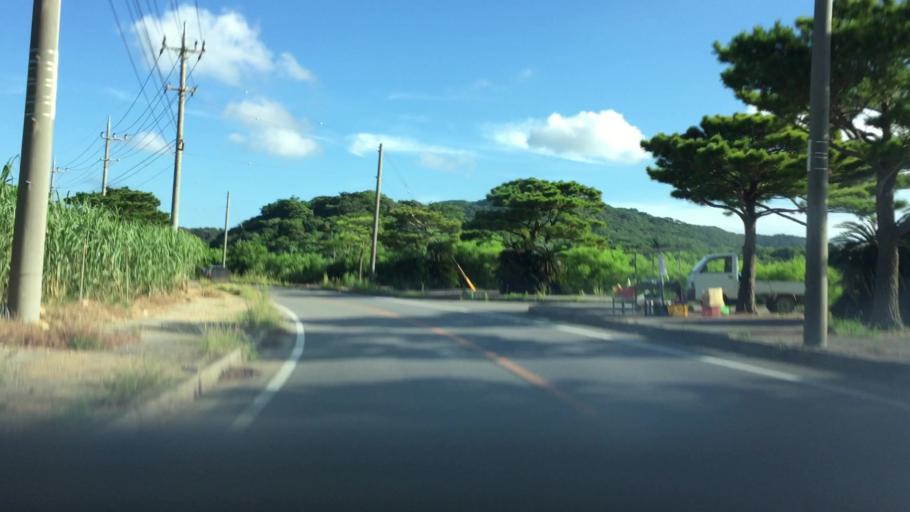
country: JP
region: Okinawa
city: Ishigaki
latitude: 24.3861
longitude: 124.1518
